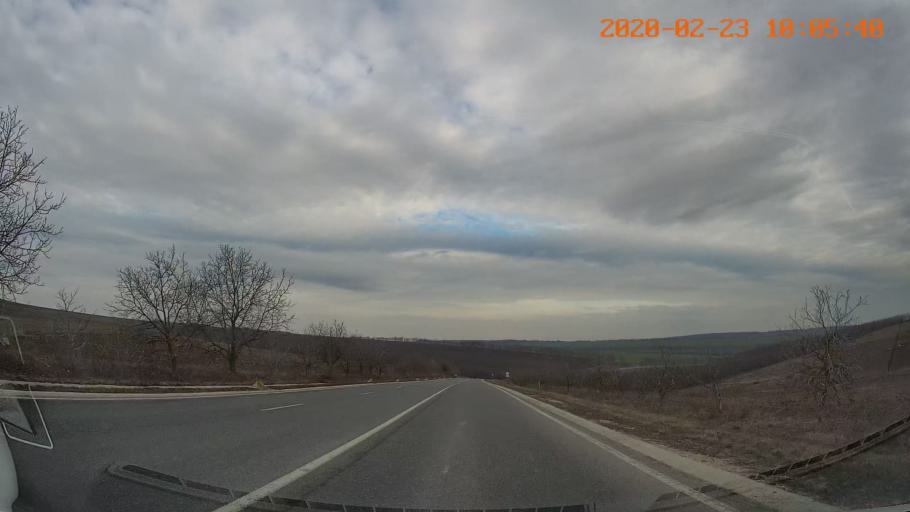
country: MD
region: Soldanesti
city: Soldanesti
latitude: 47.6922
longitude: 28.8320
